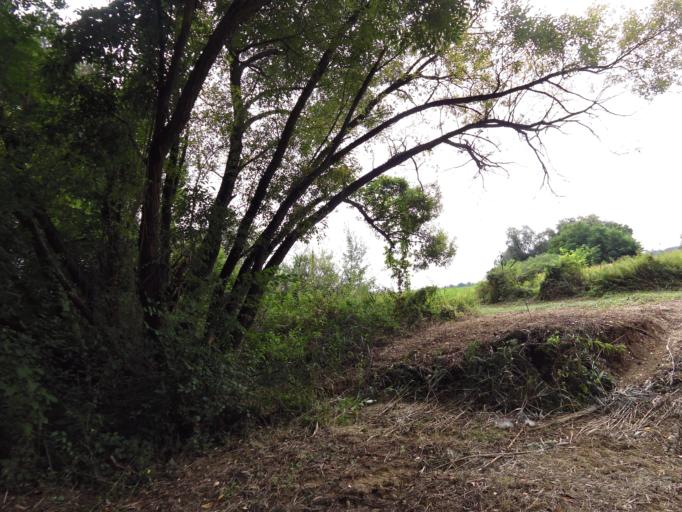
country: HU
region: Veszprem
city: Tapolca
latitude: 46.8358
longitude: 17.3680
